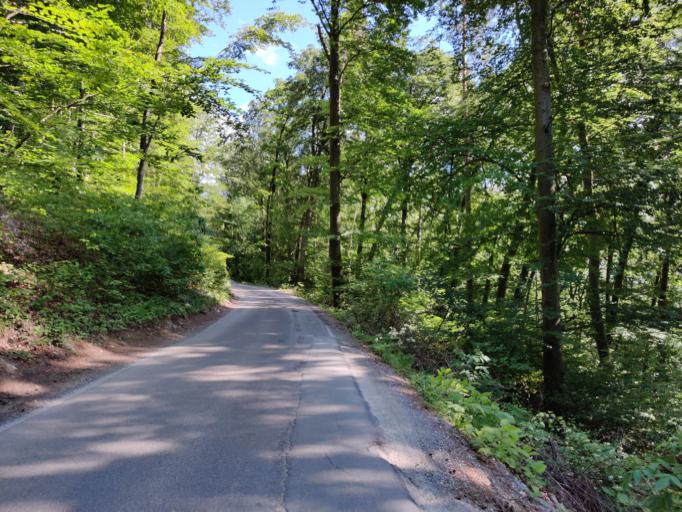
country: AT
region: Styria
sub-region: Graz Stadt
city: Wetzelsdorf
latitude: 47.0354
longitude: 15.3673
